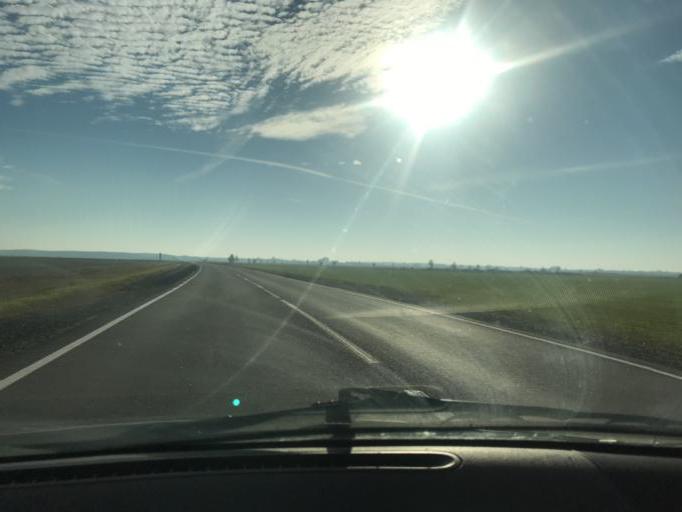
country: BY
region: Brest
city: Drahichyn
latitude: 52.1937
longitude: 25.2505
